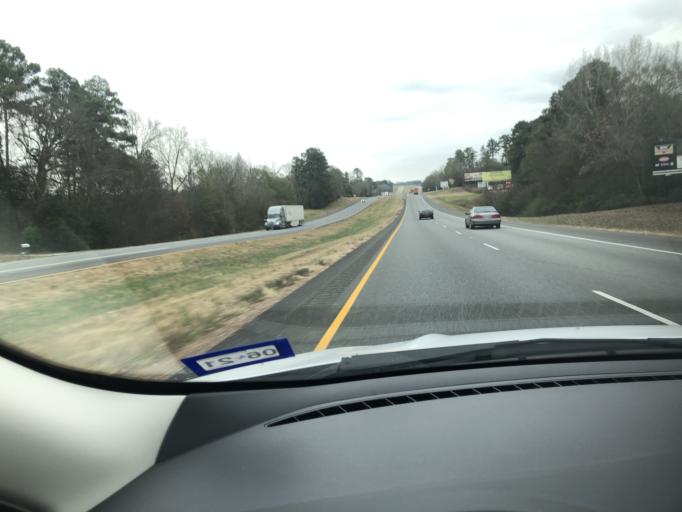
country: US
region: Texas
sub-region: Angelina County
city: Redland
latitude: 31.4284
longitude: -94.7264
